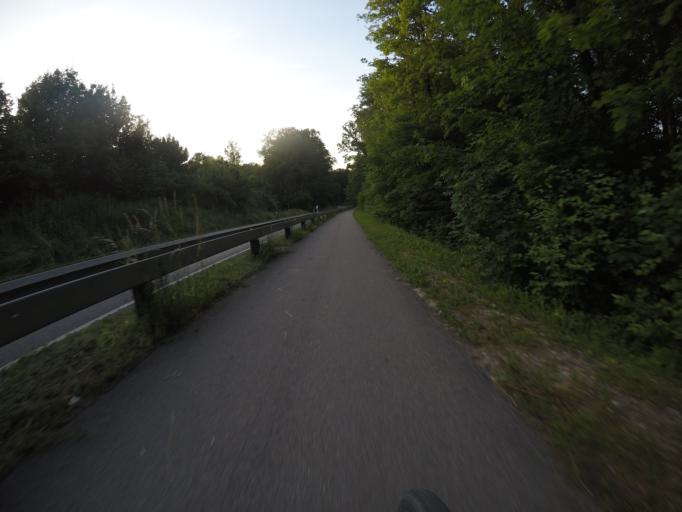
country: DE
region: Baden-Wuerttemberg
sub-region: Regierungsbezirk Stuttgart
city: Steinenbronn
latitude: 48.6708
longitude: 9.1267
